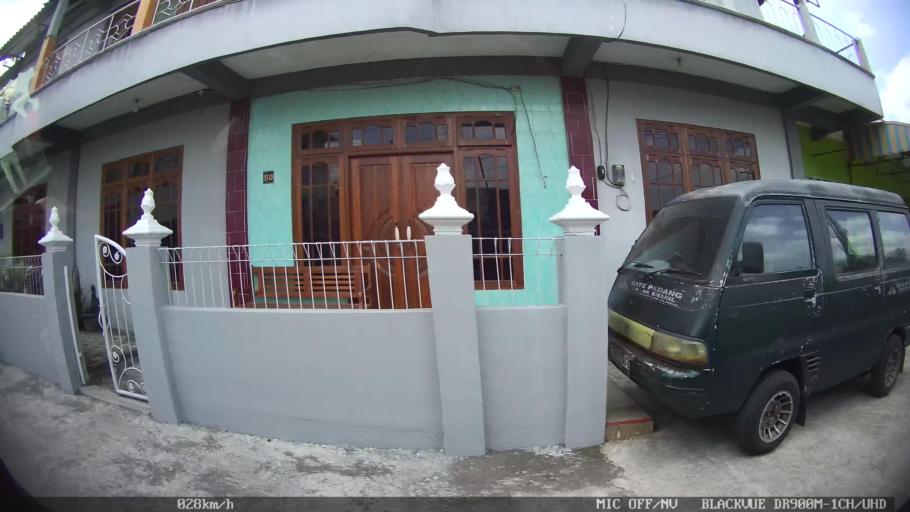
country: ID
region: Daerah Istimewa Yogyakarta
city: Kasihan
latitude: -7.8113
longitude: 110.3453
